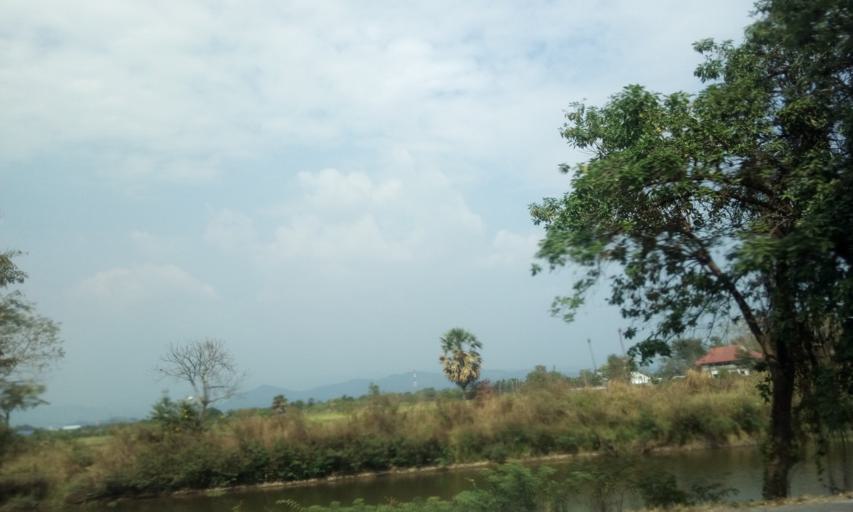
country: TH
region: Nakhon Nayok
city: Nakhon Nayok
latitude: 14.2119
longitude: 101.1760
